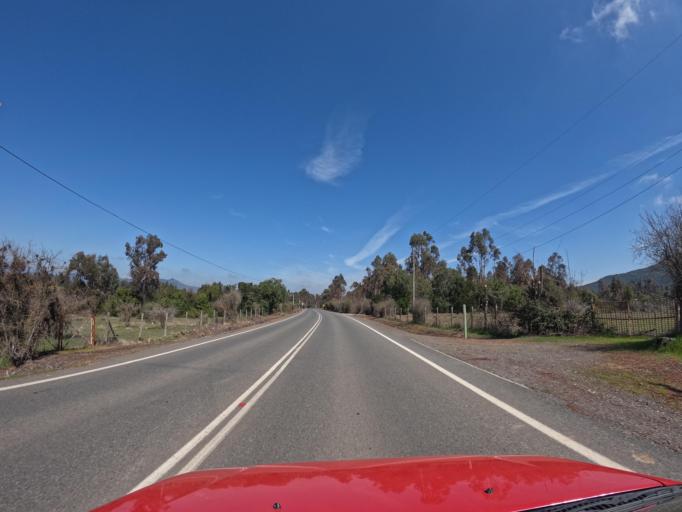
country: CL
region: Maule
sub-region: Provincia de Talca
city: San Clemente
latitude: -35.4422
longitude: -71.2656
